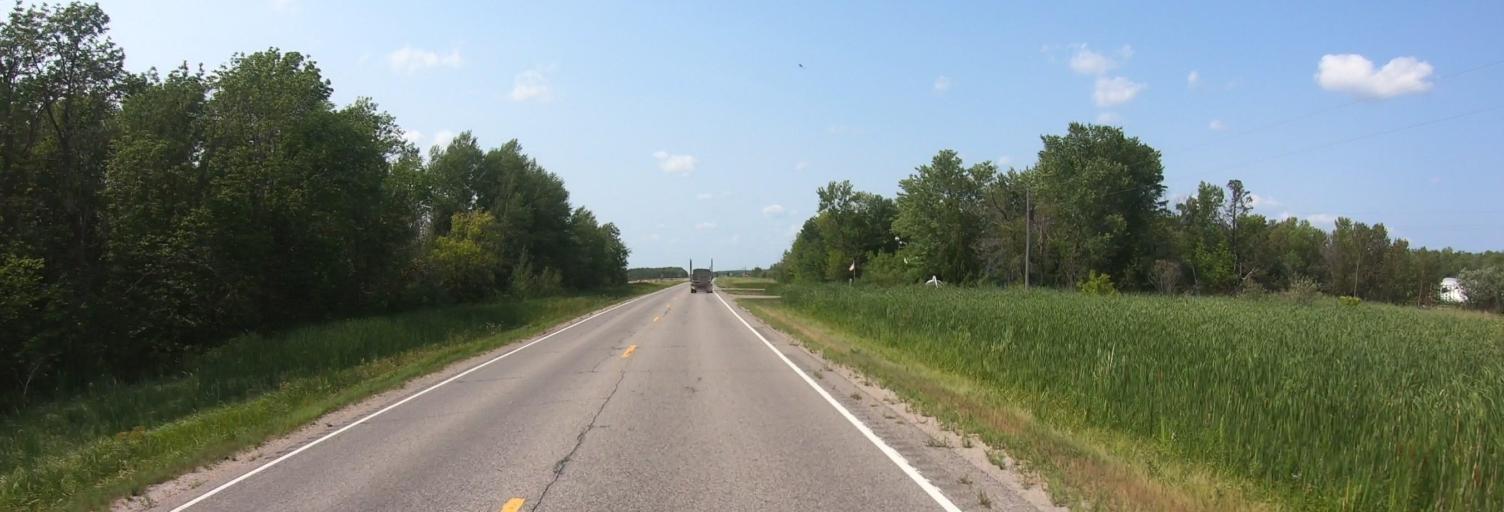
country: US
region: Minnesota
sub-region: Roseau County
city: Warroad
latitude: 48.8529
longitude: -95.2218
